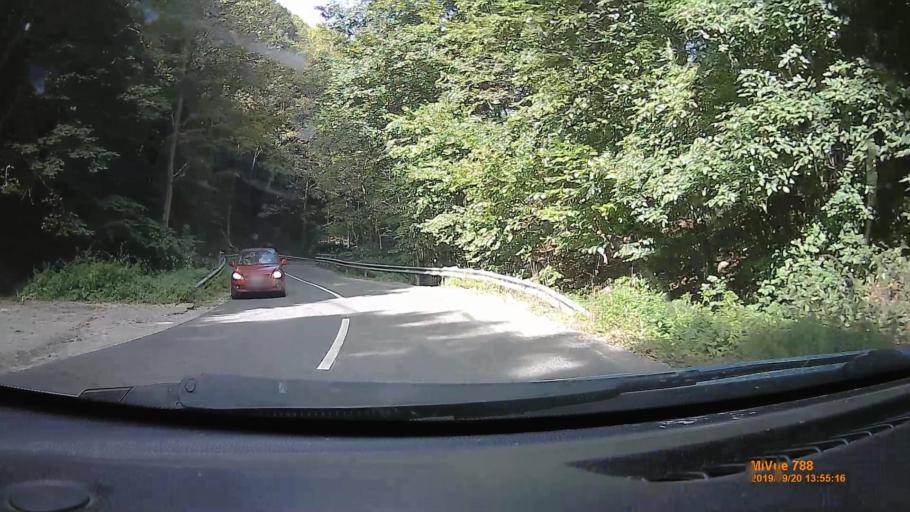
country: HU
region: Borsod-Abauj-Zemplen
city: Saly
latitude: 48.0801
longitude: 20.6160
